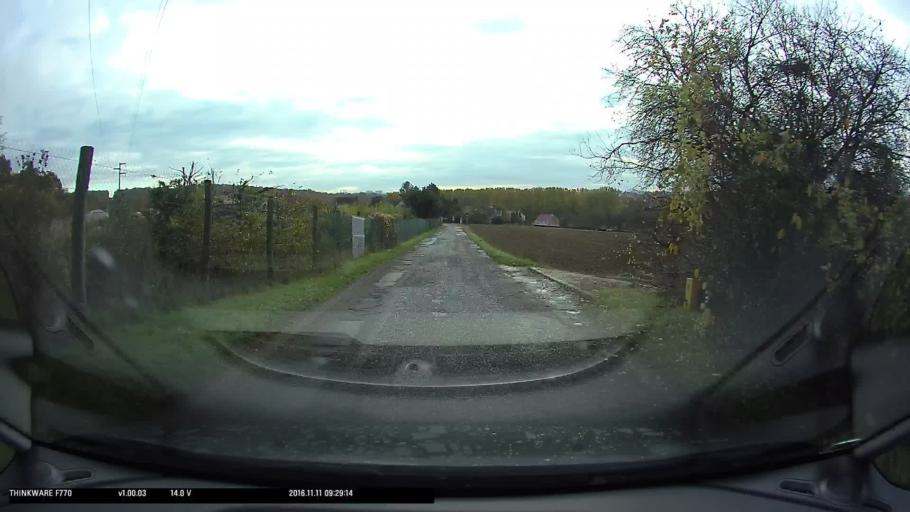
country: FR
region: Ile-de-France
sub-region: Departement du Val-d'Oise
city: Osny
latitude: 49.0697
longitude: 2.0481
